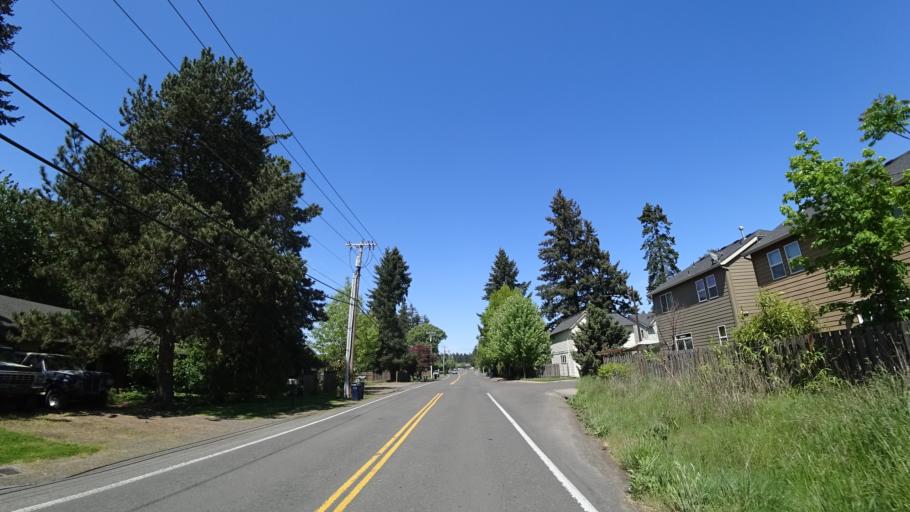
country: US
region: Oregon
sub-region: Washington County
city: Aloha
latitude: 45.4874
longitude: -122.8419
